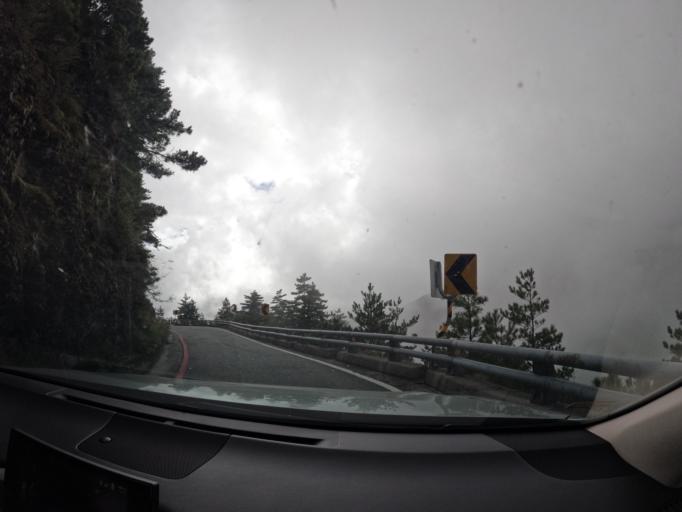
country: TW
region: Taiwan
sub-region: Taitung
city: Taitung
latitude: 23.2635
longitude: 120.9756
